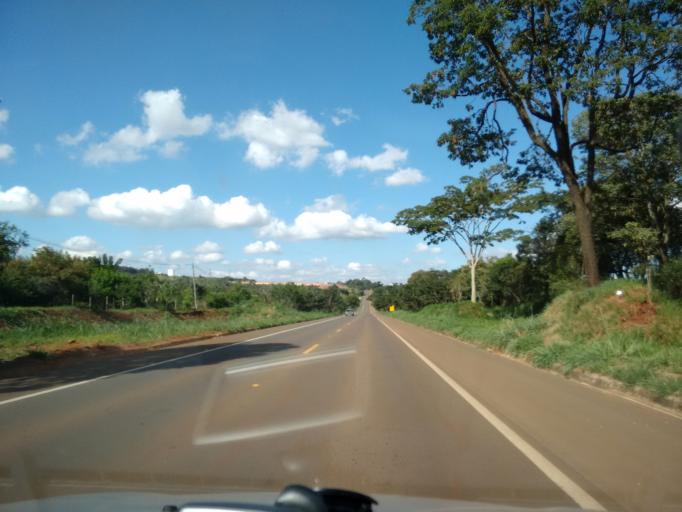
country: BR
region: Sao Paulo
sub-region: Sao Carlos
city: Sao Carlos
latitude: -22.0658
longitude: -47.9179
